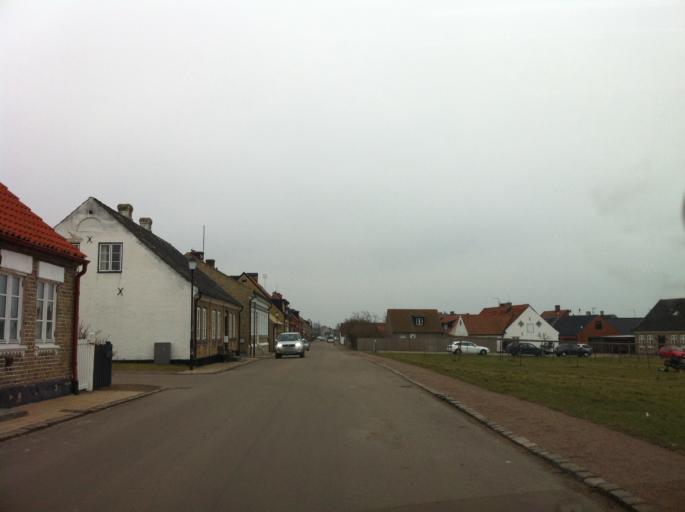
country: SE
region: Skane
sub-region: Landskrona
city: Landskrona
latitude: 55.8979
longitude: 12.8061
